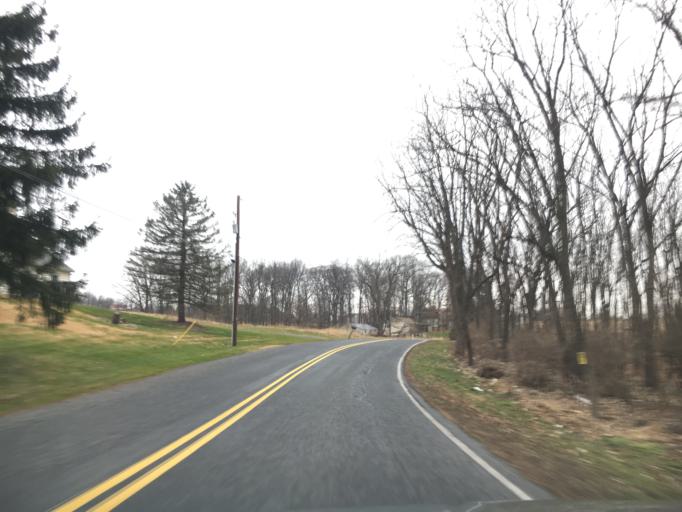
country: US
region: Pennsylvania
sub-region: Lehigh County
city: Egypt
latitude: 40.6875
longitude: -75.5660
